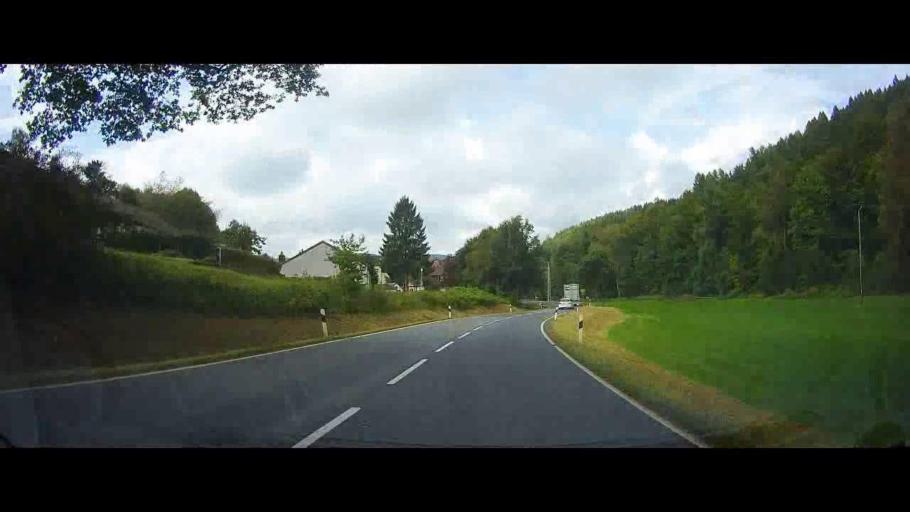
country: DE
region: Lower Saxony
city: Adelebsen
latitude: 51.6627
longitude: 9.7494
